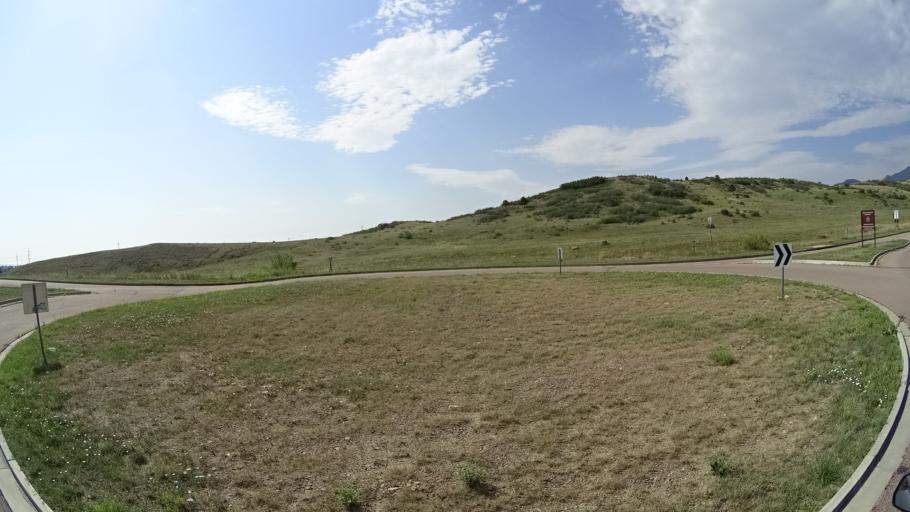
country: US
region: Colorado
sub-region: El Paso County
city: Fort Carson
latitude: 38.7382
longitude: -104.8115
